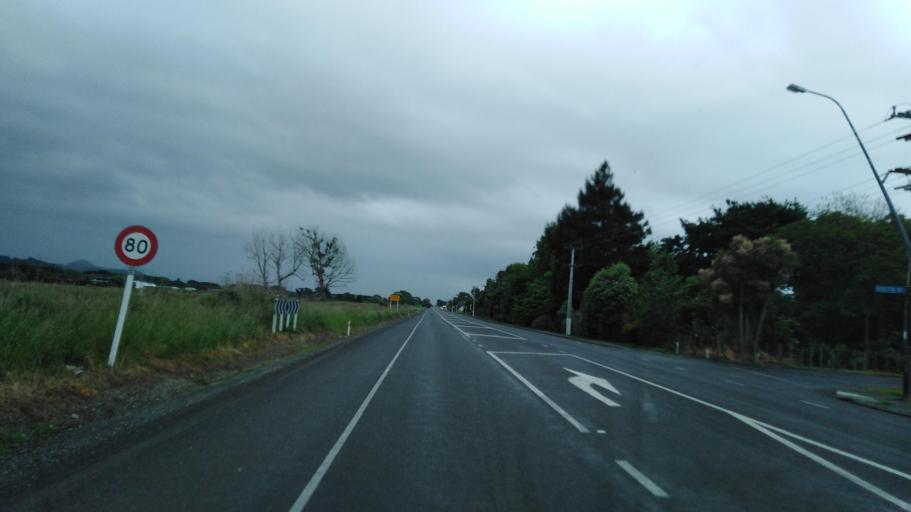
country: NZ
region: Manawatu-Wanganui
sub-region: Horowhenua District
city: Levin
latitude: -40.6425
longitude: 175.2661
